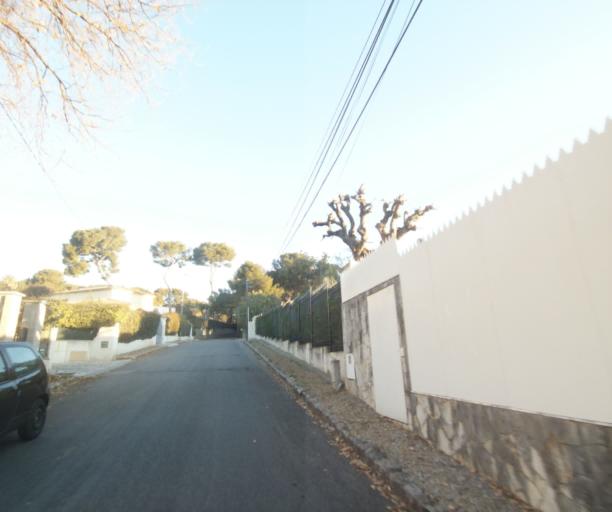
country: FR
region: Provence-Alpes-Cote d'Azur
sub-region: Departement des Alpes-Maritimes
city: Vallauris
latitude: 43.5799
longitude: 7.0846
